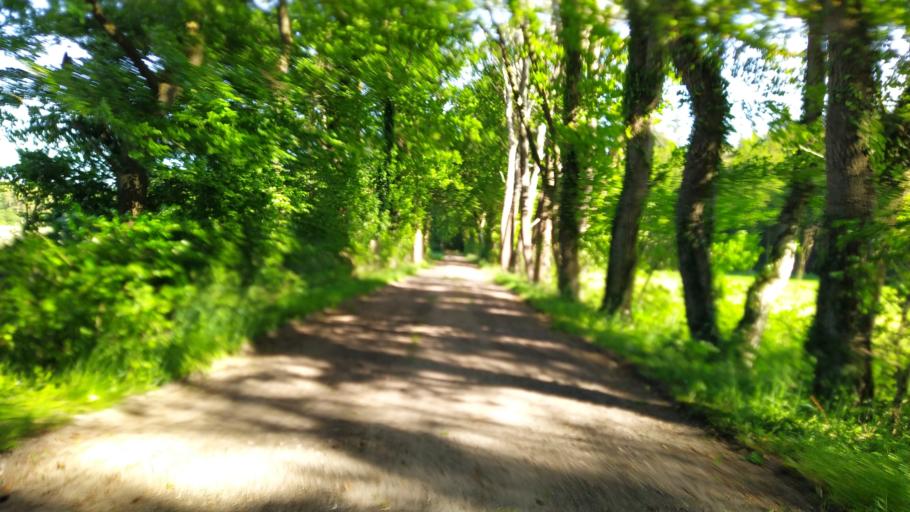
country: DE
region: Lower Saxony
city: Ahlerstedt
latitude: 53.4221
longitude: 9.4802
